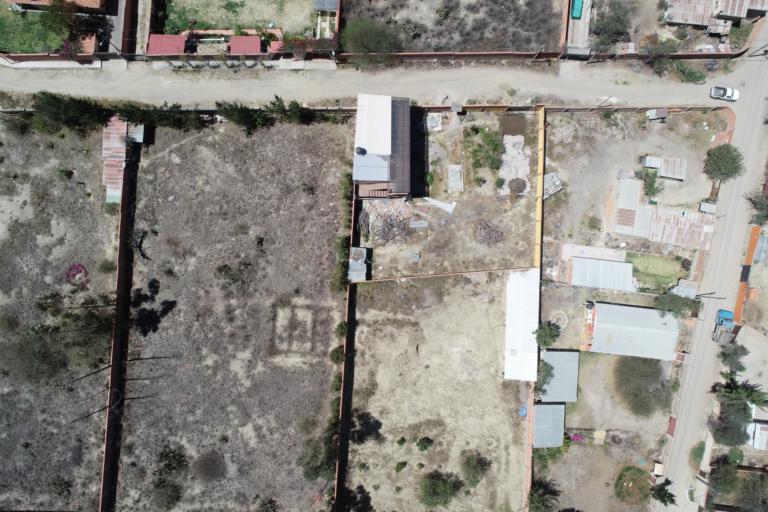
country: BO
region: La Paz
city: La Paz
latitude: -16.6290
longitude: -68.0555
